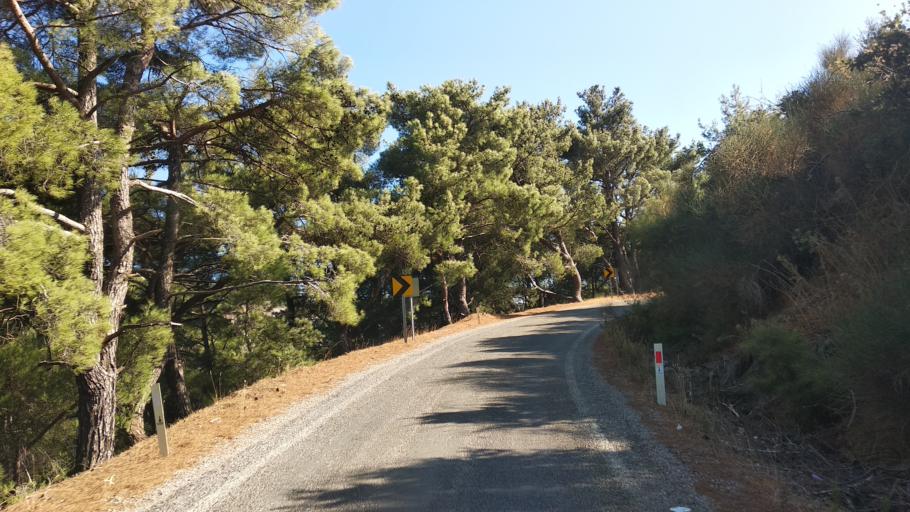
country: TR
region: Izmir
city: Gaziemir
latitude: 38.3264
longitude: 26.9559
